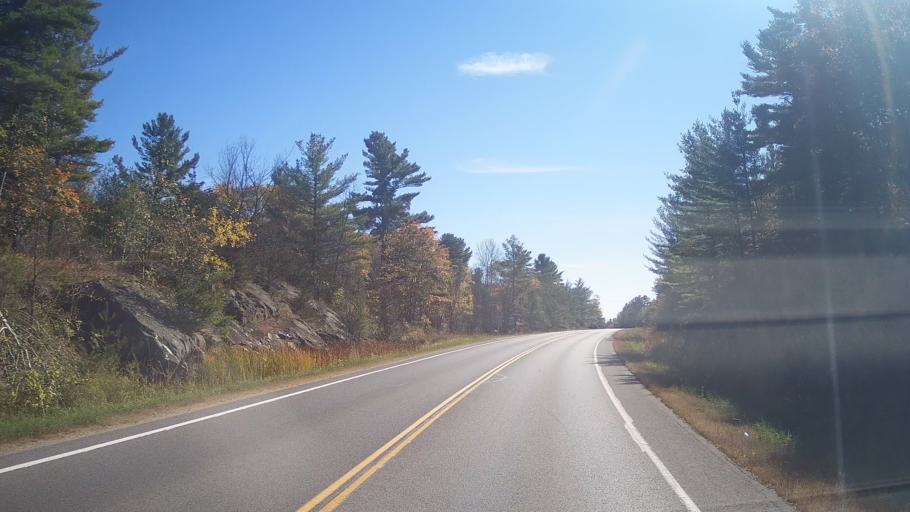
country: CA
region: Ontario
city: Skatepark
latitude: 44.6514
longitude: -76.7154
